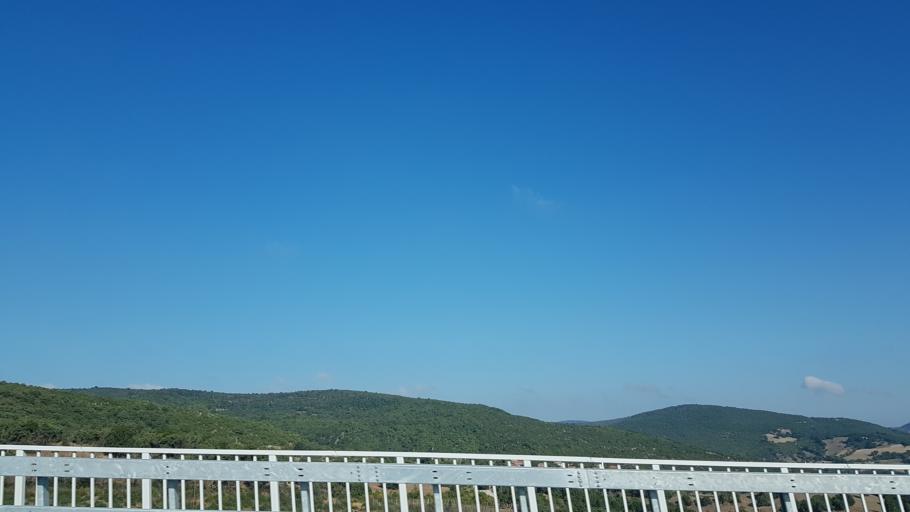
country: TR
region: Balikesir
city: Ertugrul
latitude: 39.5584
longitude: 27.7001
